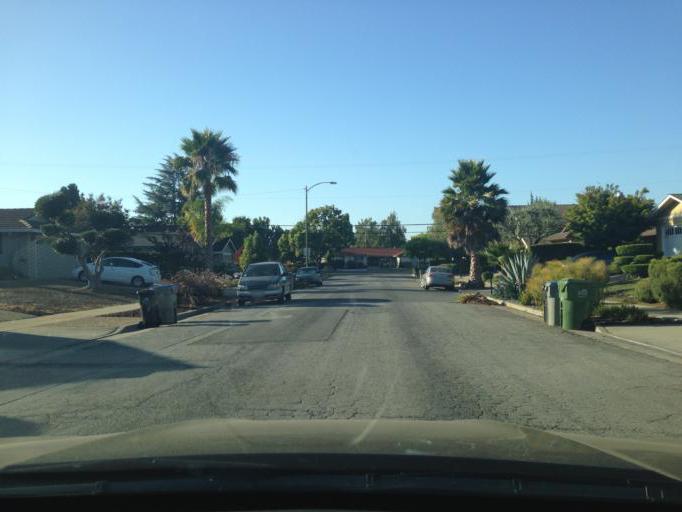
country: US
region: California
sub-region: Santa Clara County
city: Cambrian Park
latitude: 37.2210
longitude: -121.8735
